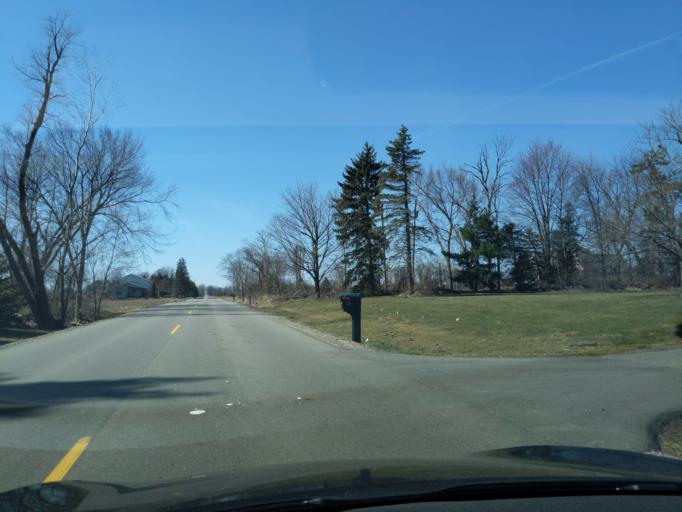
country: US
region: Michigan
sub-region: Eaton County
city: Grand Ledge
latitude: 42.7265
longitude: -84.8029
